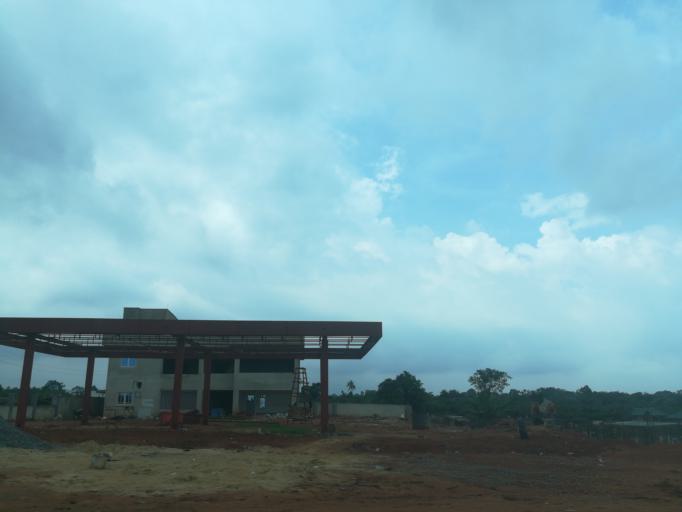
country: NG
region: Lagos
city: Ikorodu
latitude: 6.6635
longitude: 3.6223
